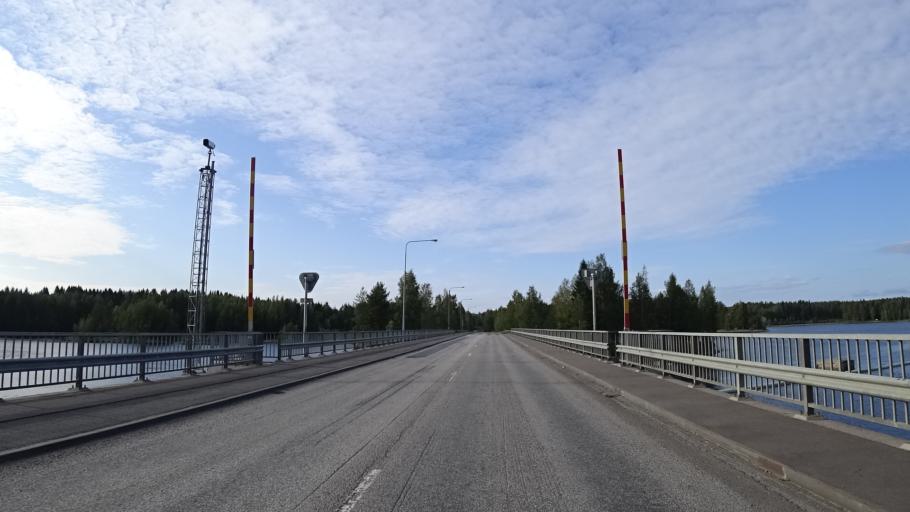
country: FI
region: North Karelia
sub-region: Joensuu
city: Eno
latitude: 62.8023
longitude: 30.1536
